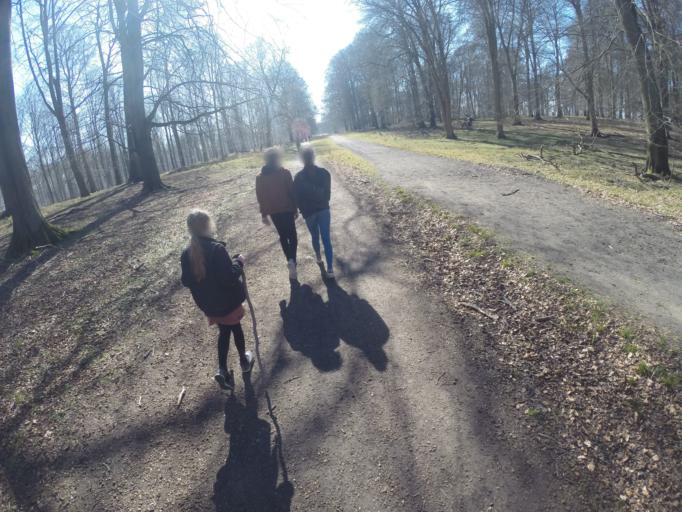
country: DK
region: Capital Region
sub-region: Lyngby-Tarbaek Kommune
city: Kongens Lyngby
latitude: 55.7791
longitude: 12.5499
